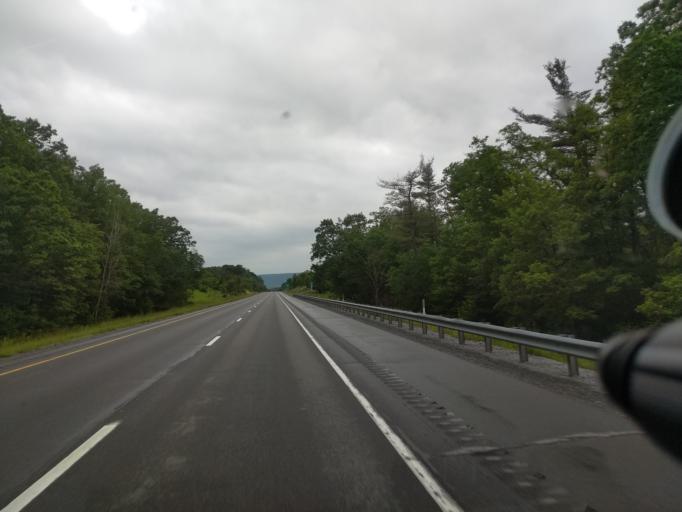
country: US
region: Pennsylvania
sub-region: Clinton County
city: Avis
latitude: 41.0548
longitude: -77.2812
